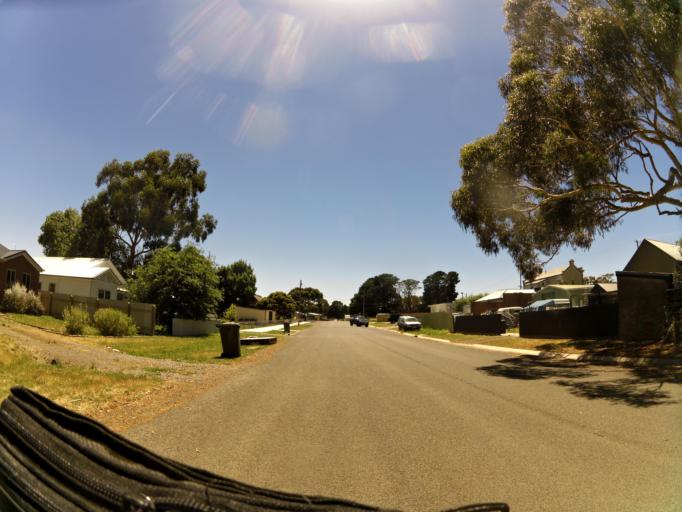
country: AU
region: Victoria
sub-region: Ballarat North
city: Delacombe
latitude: -37.6443
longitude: 143.6839
